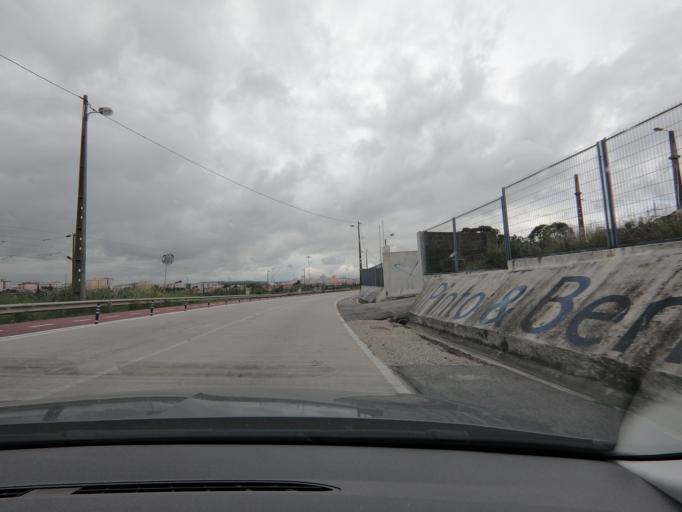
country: PT
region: Lisbon
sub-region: Sintra
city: Sintra
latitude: 38.8008
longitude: -9.3599
